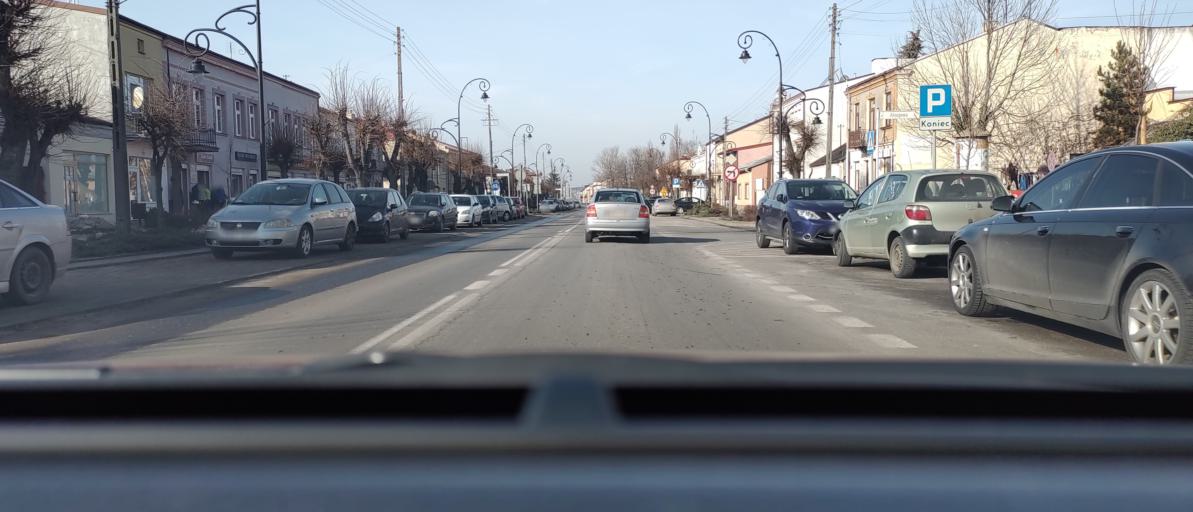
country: PL
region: Masovian Voivodeship
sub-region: Powiat bialobrzeski
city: Bialobrzegi
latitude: 51.6486
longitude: 20.9550
